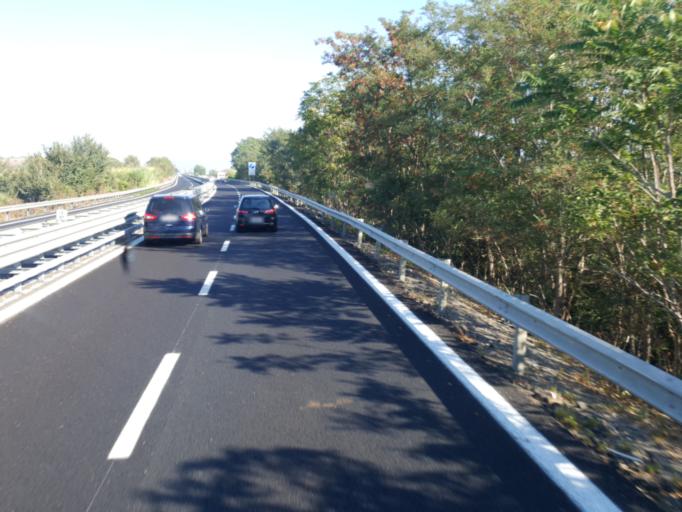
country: IT
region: Latium
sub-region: Provincia di Viterbo
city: Tarquinia
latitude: 42.2824
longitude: 11.6930
